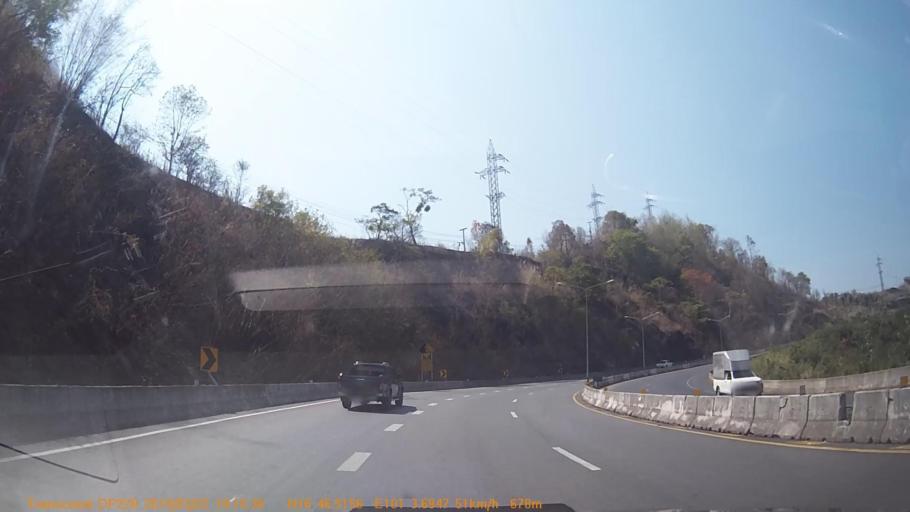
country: TH
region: Phetchabun
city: Khao Kho
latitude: 16.7750
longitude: 101.0614
